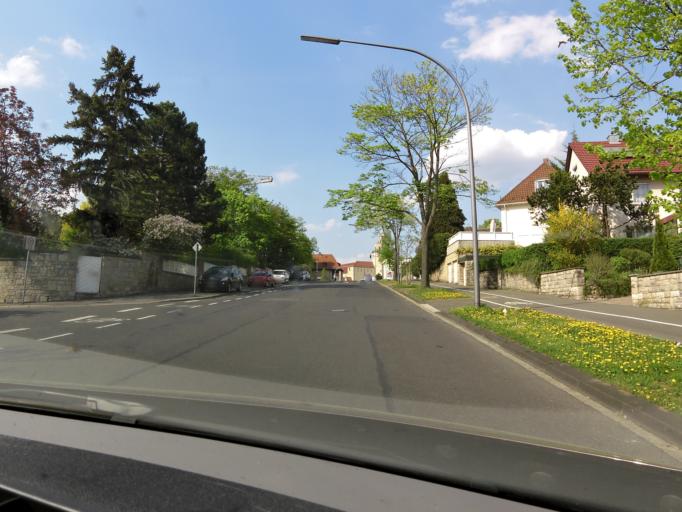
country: DE
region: Bavaria
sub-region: Regierungsbezirk Unterfranken
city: Wuerzburg
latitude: 49.7902
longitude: 9.9531
